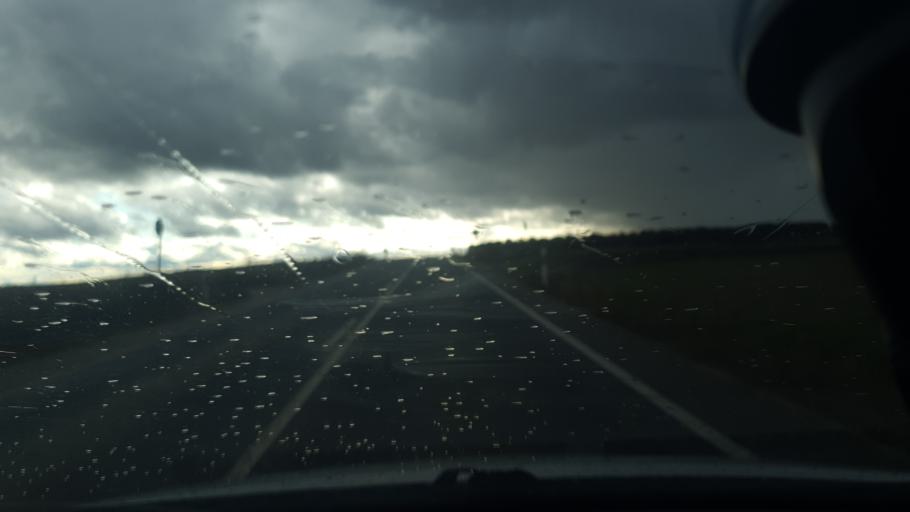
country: ES
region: Castille and Leon
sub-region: Provincia de Segovia
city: Chane
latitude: 41.3146
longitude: -4.3910
